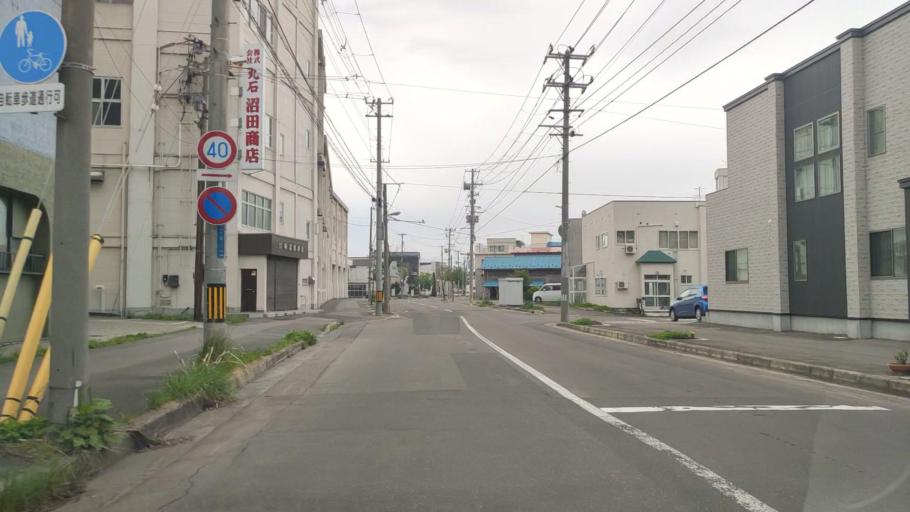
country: JP
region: Aomori
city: Aomori Shi
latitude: 40.8288
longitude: 140.7592
